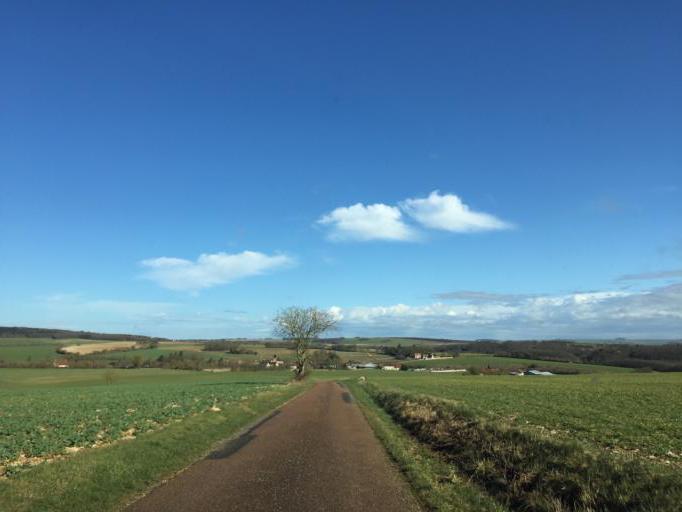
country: FR
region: Bourgogne
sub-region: Departement de l'Yonne
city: Fontenailles
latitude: 47.5513
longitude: 3.3305
